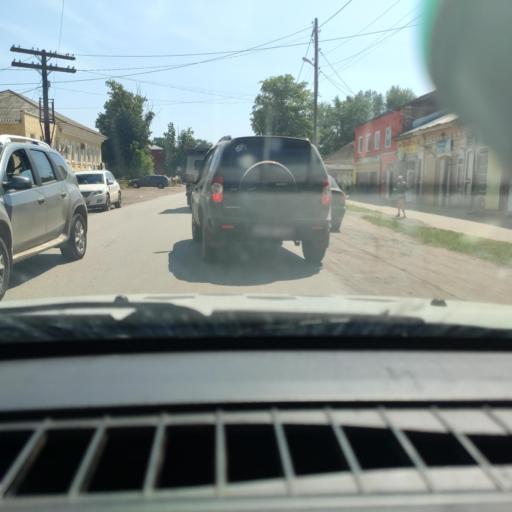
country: RU
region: Perm
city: Okhansk
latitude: 57.7226
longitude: 55.3907
